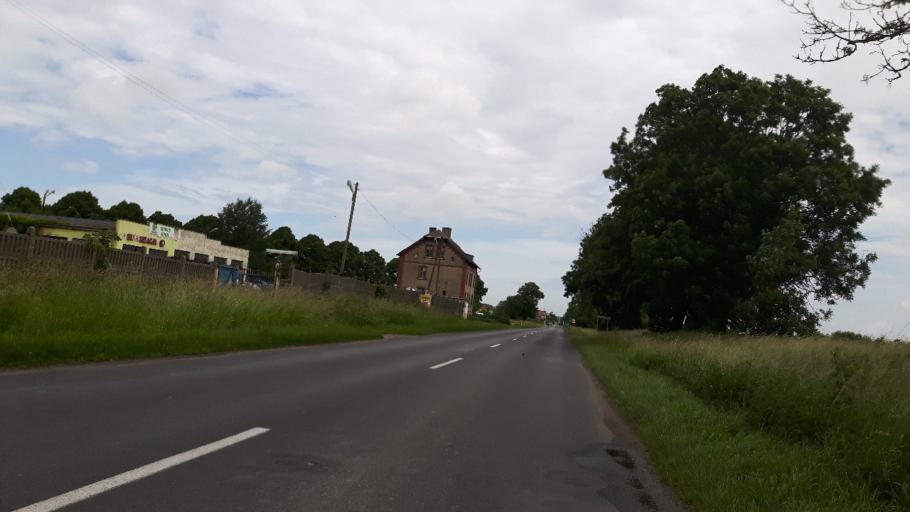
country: PL
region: West Pomeranian Voivodeship
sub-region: Powiat gryficki
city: Trzebiatow
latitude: 54.0459
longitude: 15.2521
